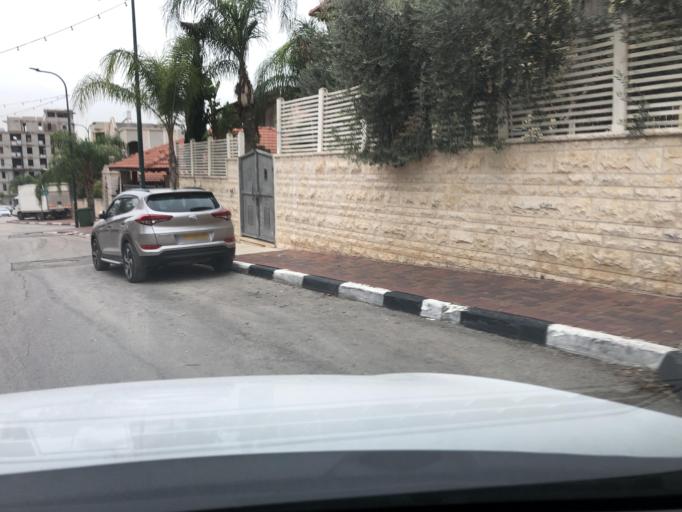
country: IL
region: Central District
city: Kafr Qasim
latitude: 32.1305
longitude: 34.9669
